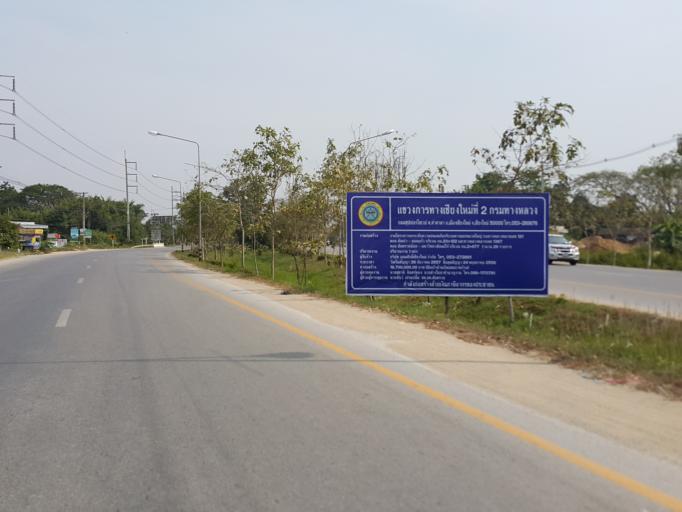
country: TH
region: Chiang Mai
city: San Sai
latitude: 18.8335
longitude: 99.0375
